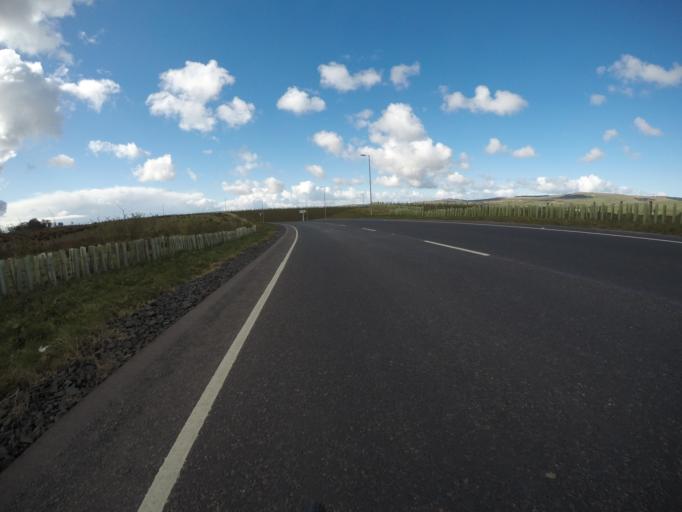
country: GB
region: Scotland
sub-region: North Ayrshire
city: Dalry
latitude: 55.7132
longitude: -4.6914
